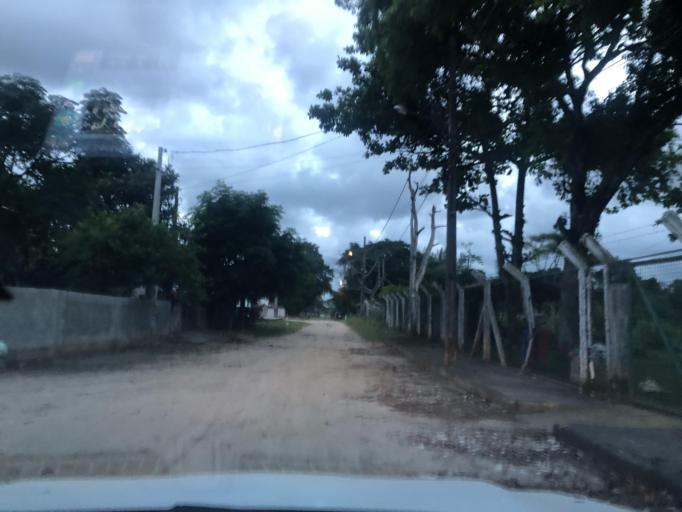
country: BR
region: Santa Catarina
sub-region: Sao Francisco Do Sul
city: Sao Francisco do Sul
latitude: -26.2280
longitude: -48.5262
